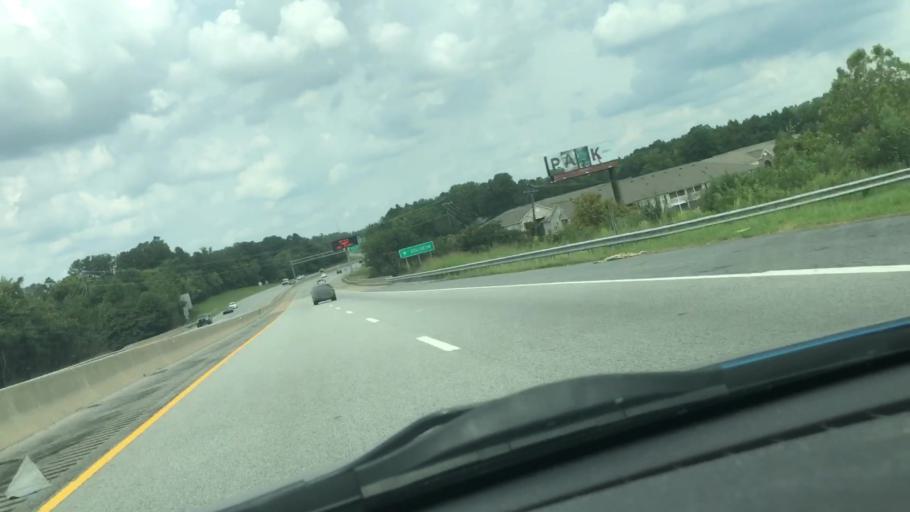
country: US
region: North Carolina
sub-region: Guilford County
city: Greensboro
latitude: 36.0200
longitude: -79.8261
